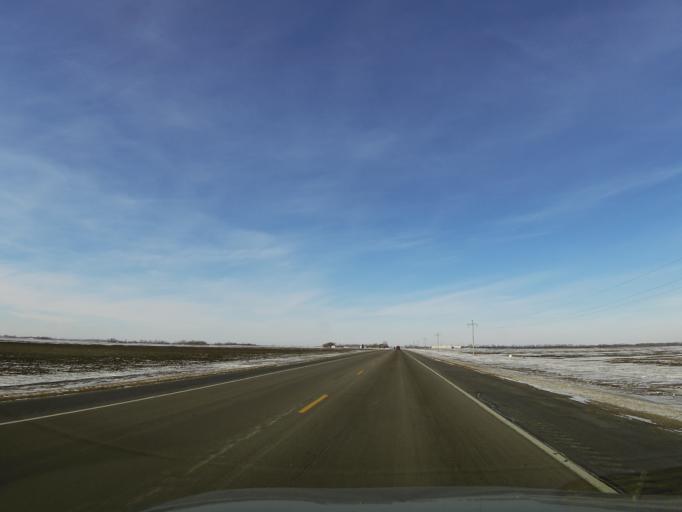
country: US
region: North Dakota
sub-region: Walsh County
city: Grafton
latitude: 48.4124
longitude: -97.3262
